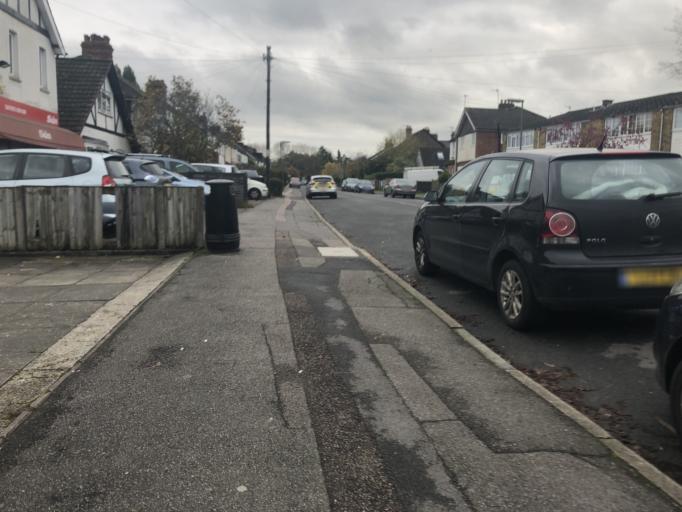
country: GB
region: England
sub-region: Surrey
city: Salfords
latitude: 51.2043
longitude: -0.1666
